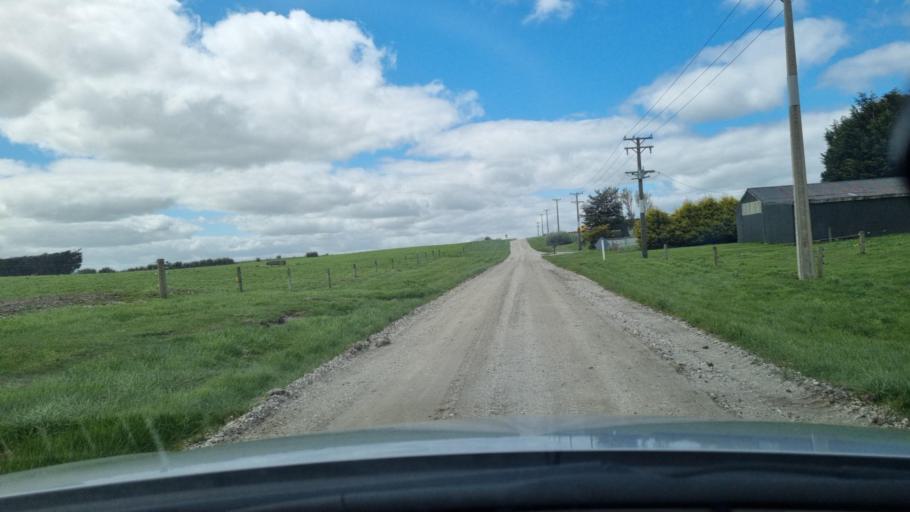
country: NZ
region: Southland
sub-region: Invercargill City
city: Invercargill
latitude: -46.4506
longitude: 168.4135
